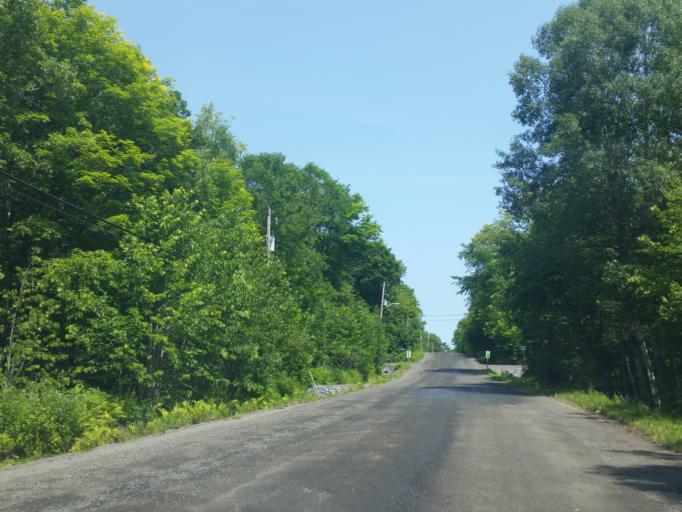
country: CA
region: Ontario
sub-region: Parry Sound District
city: Parry Sound
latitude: 45.4339
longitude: -80.0063
